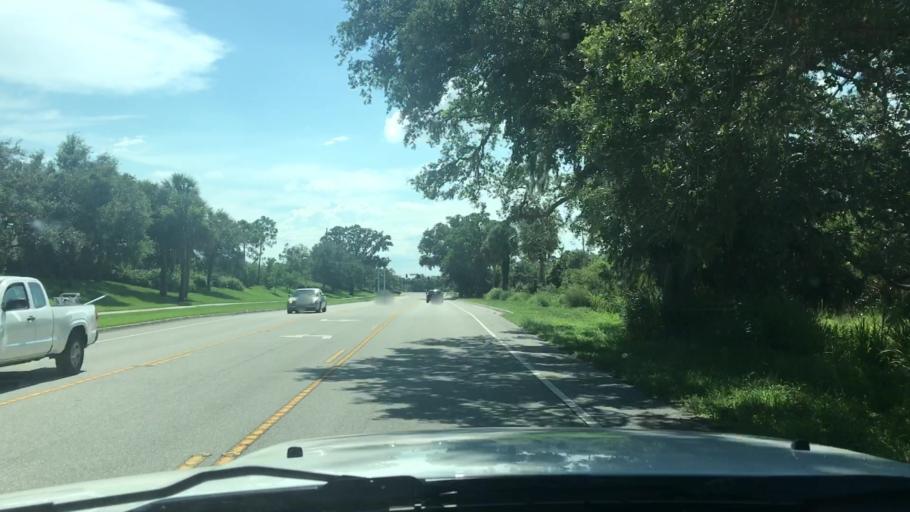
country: US
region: Florida
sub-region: Indian River County
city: Florida Ridge
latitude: 27.5722
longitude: -80.4113
